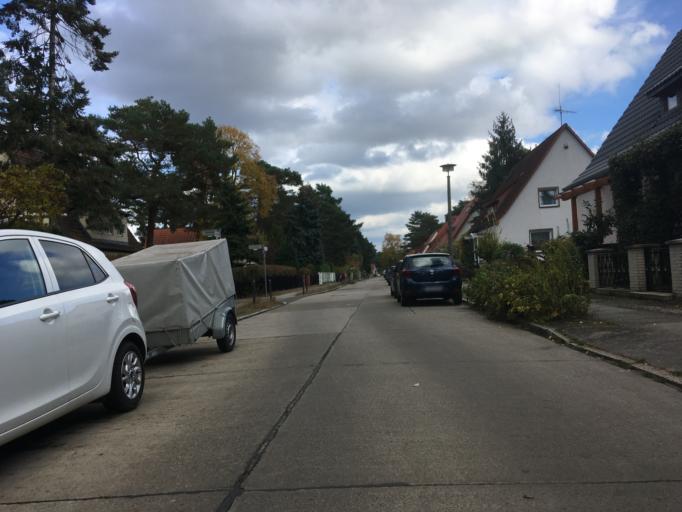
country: DE
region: Berlin
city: Oberschoneweide
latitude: 52.4485
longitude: 13.5338
